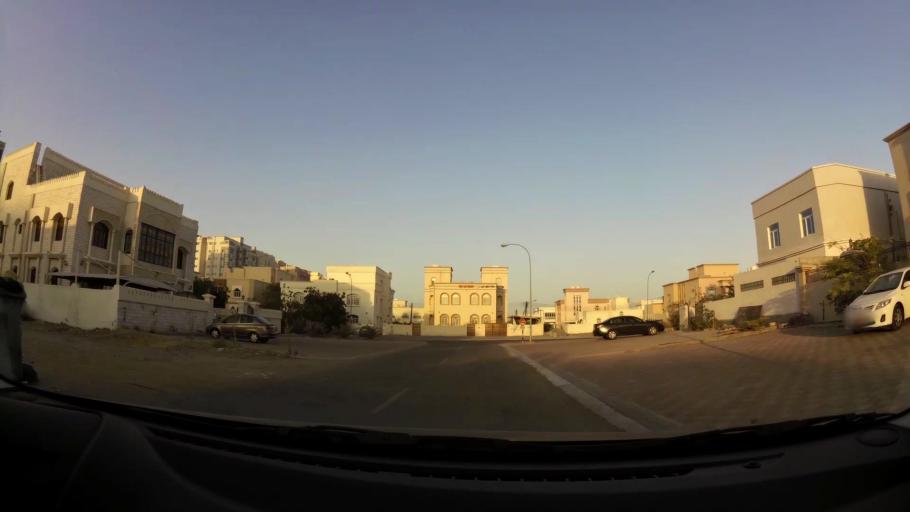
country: OM
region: Muhafazat Masqat
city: As Sib al Jadidah
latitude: 23.6141
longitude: 58.2017
